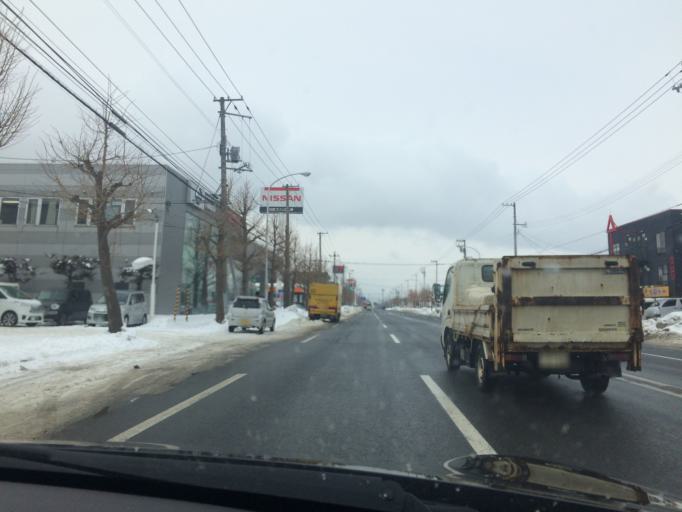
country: JP
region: Hokkaido
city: Sapporo
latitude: 43.0531
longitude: 141.4453
